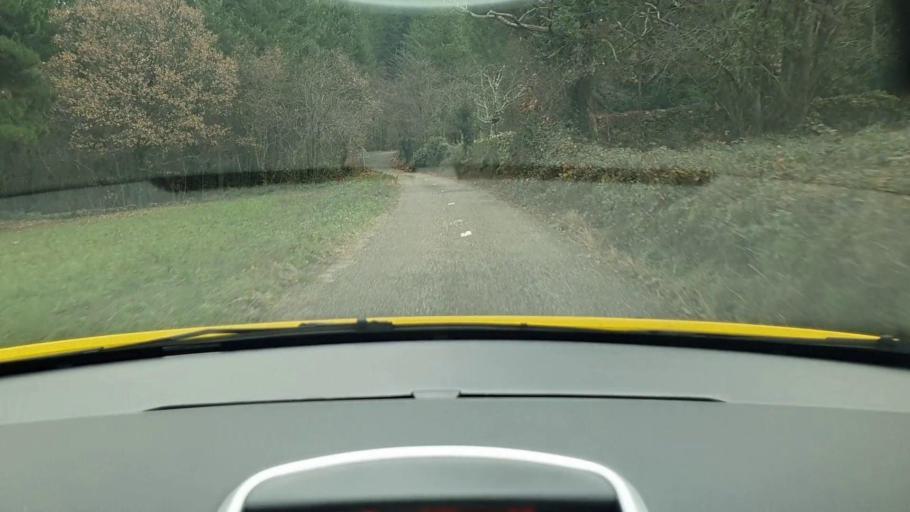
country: FR
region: Languedoc-Roussillon
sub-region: Departement du Gard
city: Besseges
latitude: 44.3508
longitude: 4.0189
